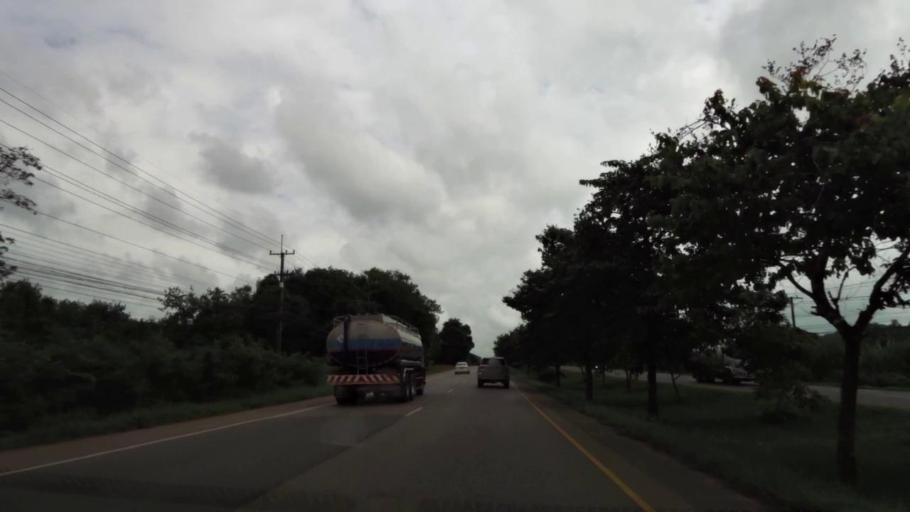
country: TH
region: Chanthaburi
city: Na Yai Am
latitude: 12.7359
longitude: 101.8984
